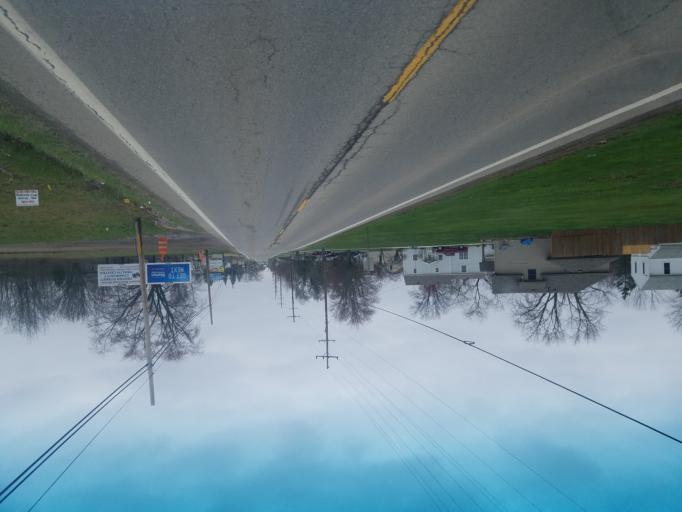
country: US
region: Ohio
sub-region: Marion County
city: Marion
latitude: 40.5559
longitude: -83.1439
